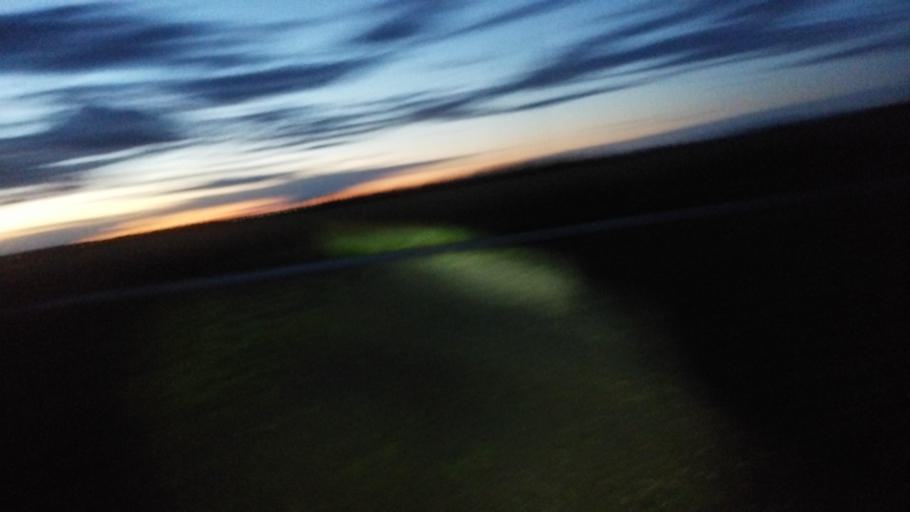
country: DE
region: Hesse
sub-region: Regierungsbezirk Darmstadt
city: Gross-Rohrheim
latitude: 49.7041
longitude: 8.5069
